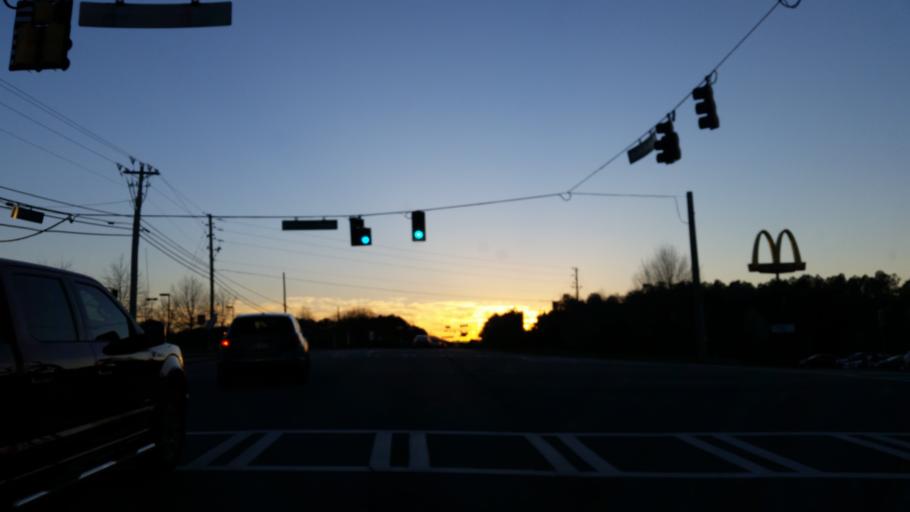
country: US
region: Georgia
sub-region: Forsyth County
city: Cumming
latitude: 34.2530
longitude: -84.0885
